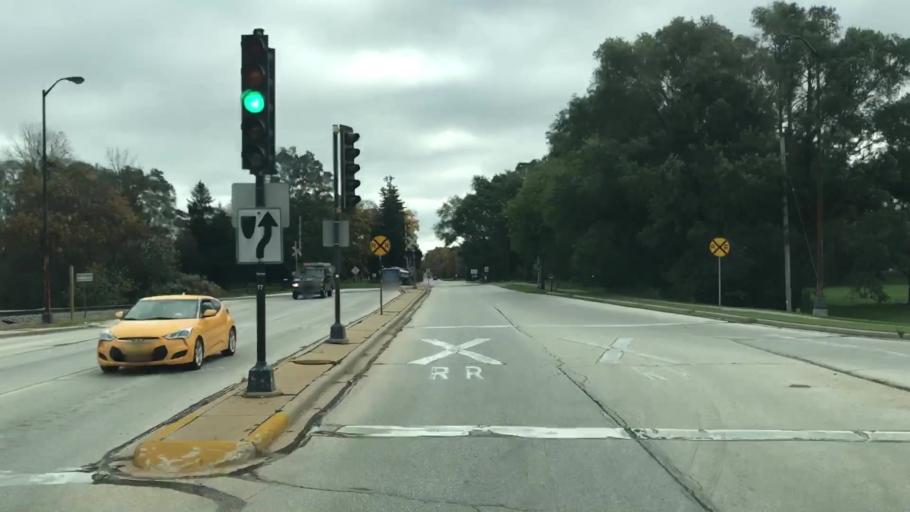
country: US
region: Wisconsin
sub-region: Waukesha County
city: Brookfield
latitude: 43.0605
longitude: -88.1093
